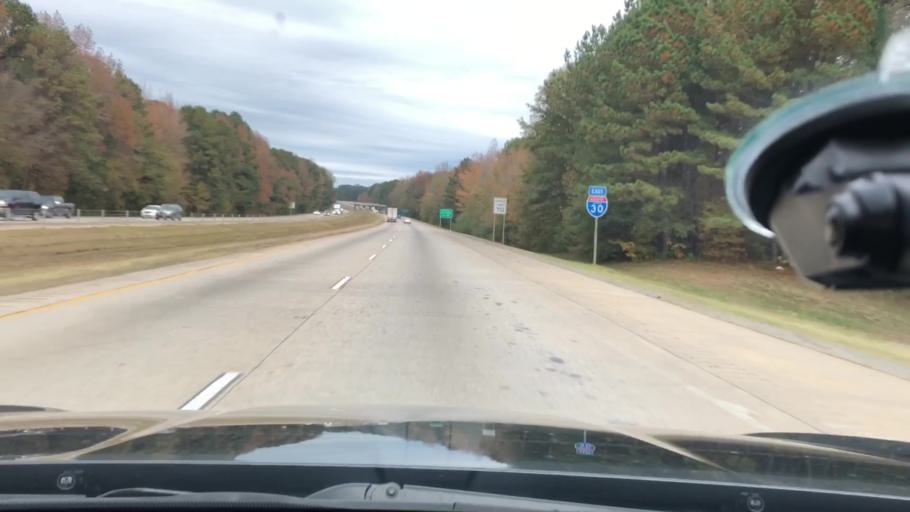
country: US
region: Arkansas
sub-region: Hot Spring County
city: Malvern
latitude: 34.4003
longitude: -92.8217
